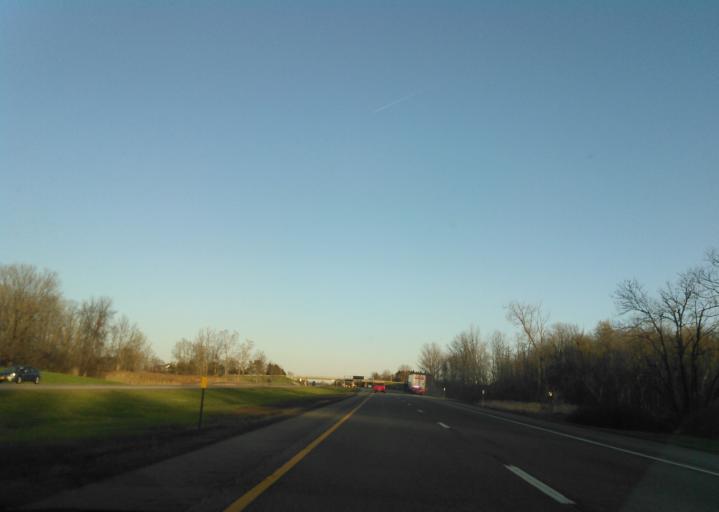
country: US
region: New York
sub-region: Monroe County
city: Pittsford
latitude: 43.0245
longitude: -77.5023
